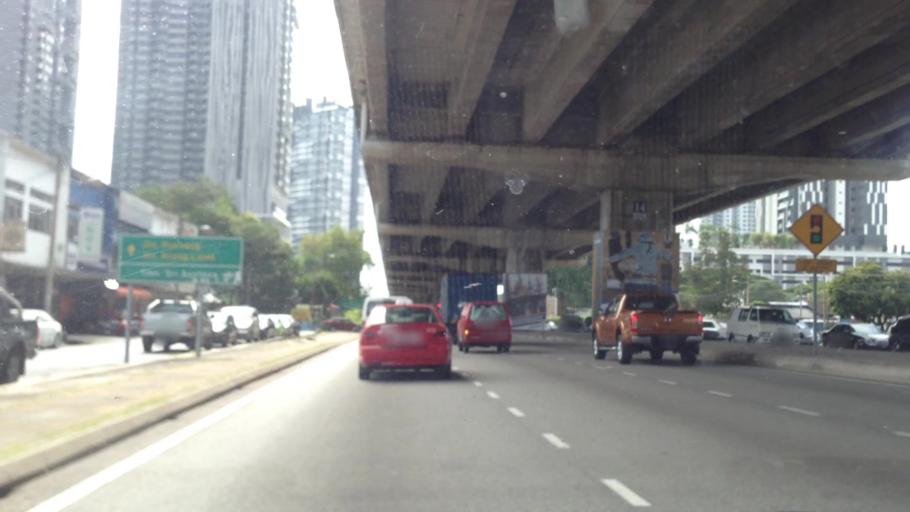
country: MY
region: Selangor
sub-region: Petaling
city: Petaling Jaya
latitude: 3.0824
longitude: 101.6587
